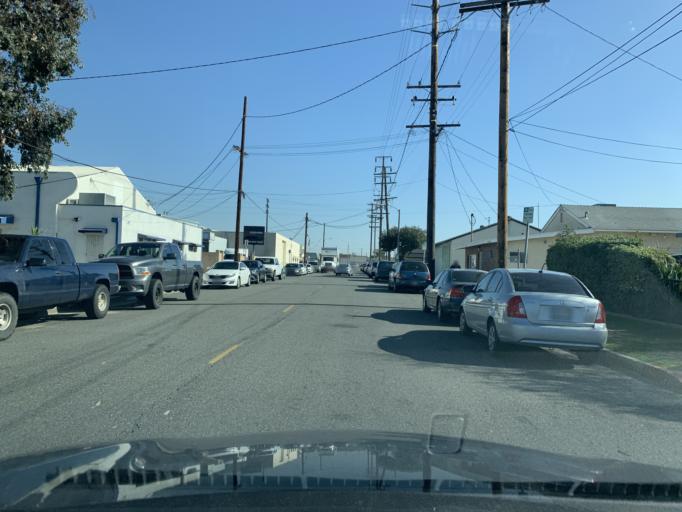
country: US
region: California
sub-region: Los Angeles County
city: Covina
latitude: 34.0916
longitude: -117.8833
